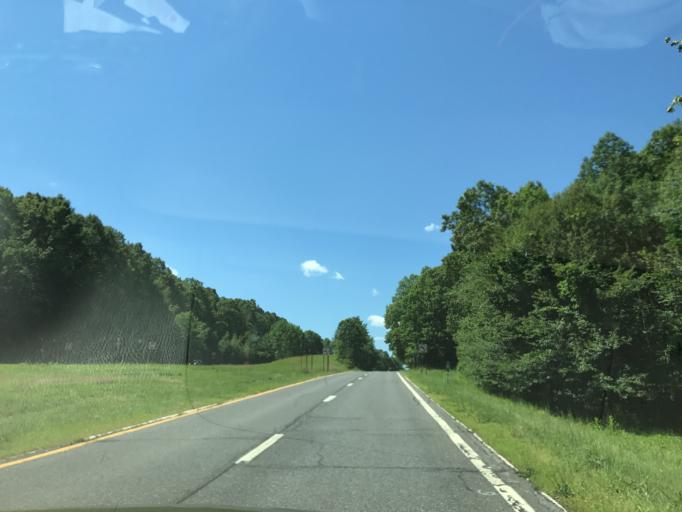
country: US
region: New York
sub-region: Dutchess County
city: Pine Plains
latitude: 41.9353
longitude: -73.7551
